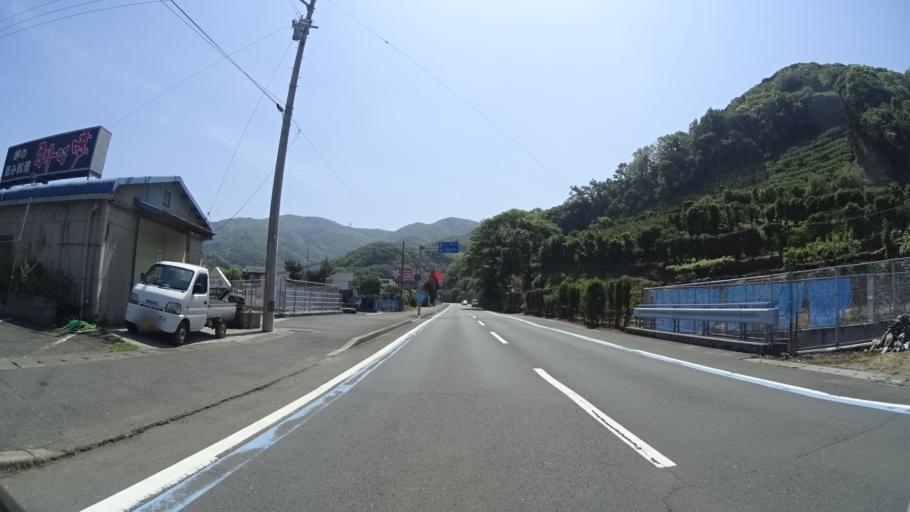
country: JP
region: Ehime
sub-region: Nishiuwa-gun
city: Ikata-cho
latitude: 33.3870
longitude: 132.1236
